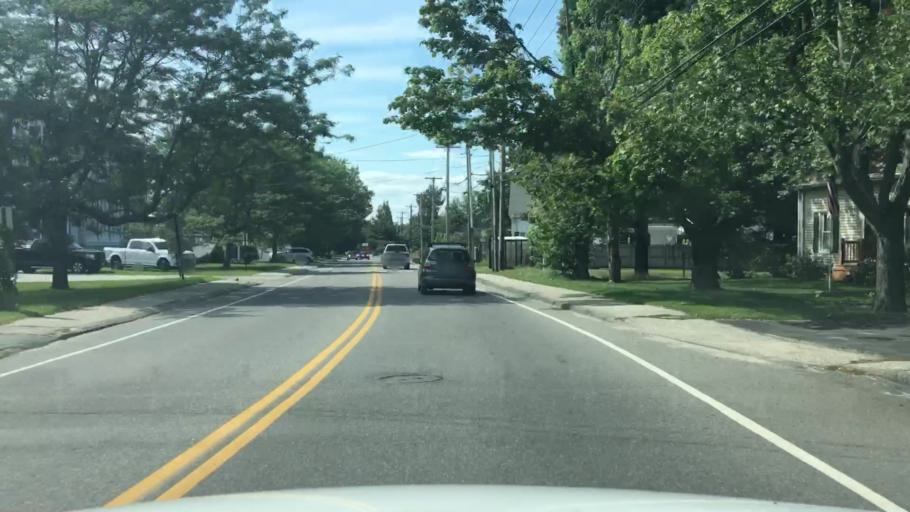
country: US
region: Maine
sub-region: Cumberland County
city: South Portland Gardens
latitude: 43.6298
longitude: -70.2867
